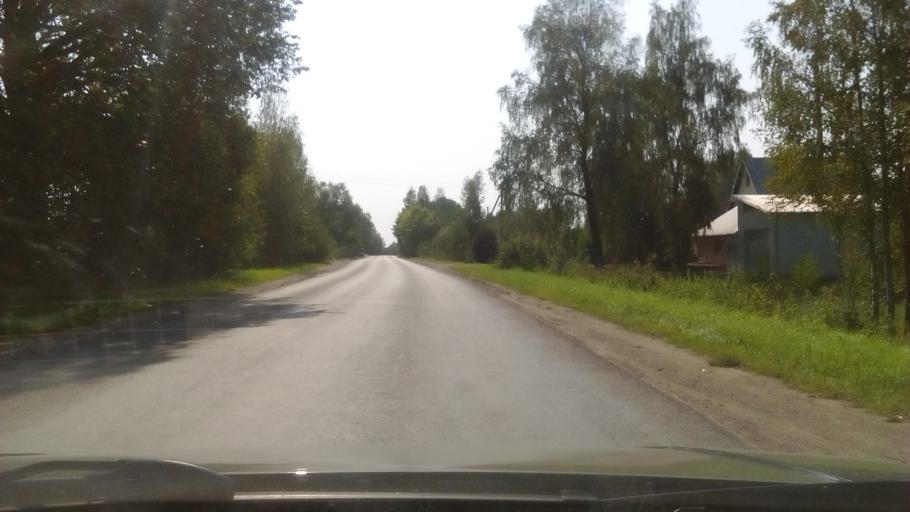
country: LT
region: Alytaus apskritis
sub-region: Alytus
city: Alytus
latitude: 54.4307
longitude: 24.0342
